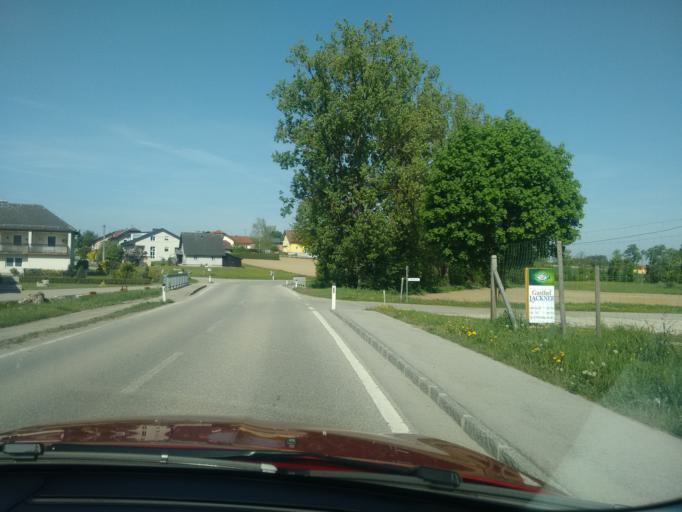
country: AT
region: Upper Austria
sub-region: Politischer Bezirk Grieskirchen
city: Bad Schallerbach
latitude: 48.3026
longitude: 13.9232
